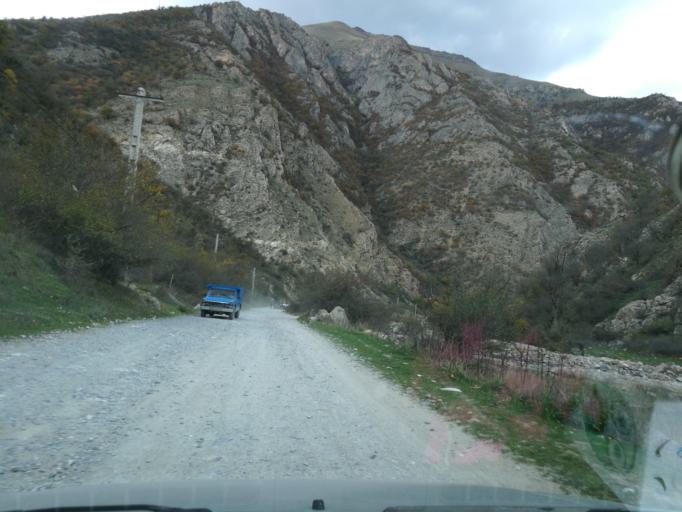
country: IR
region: Mazandaran
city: `Abbasabad
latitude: 36.4437
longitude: 51.0639
